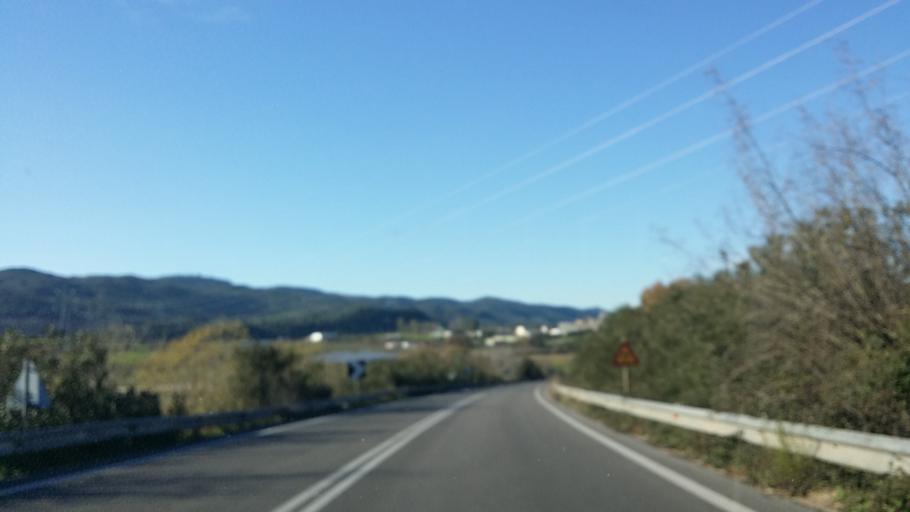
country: GR
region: West Greece
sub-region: Nomos Aitolias kai Akarnanias
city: Fitiai
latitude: 38.6897
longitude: 21.2280
